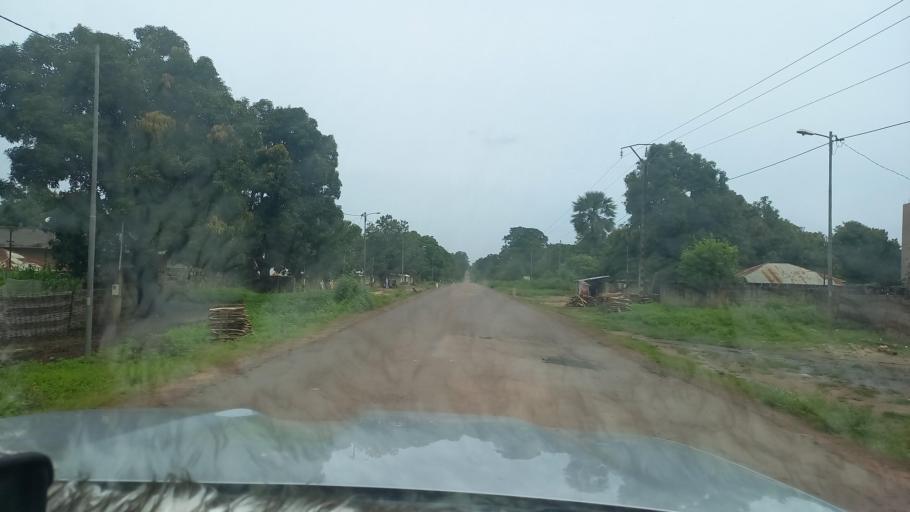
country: SN
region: Ziguinchor
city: Bignona
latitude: 12.8203
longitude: -16.1797
